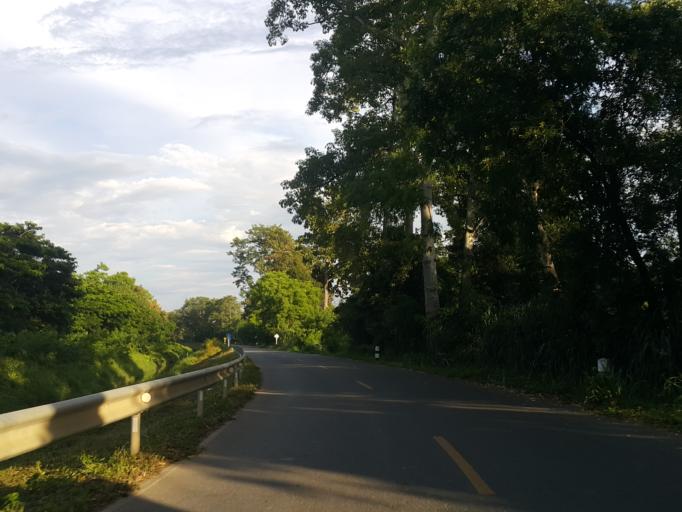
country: TH
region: Chiang Mai
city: San Sai
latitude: 18.9192
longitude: 99.0016
